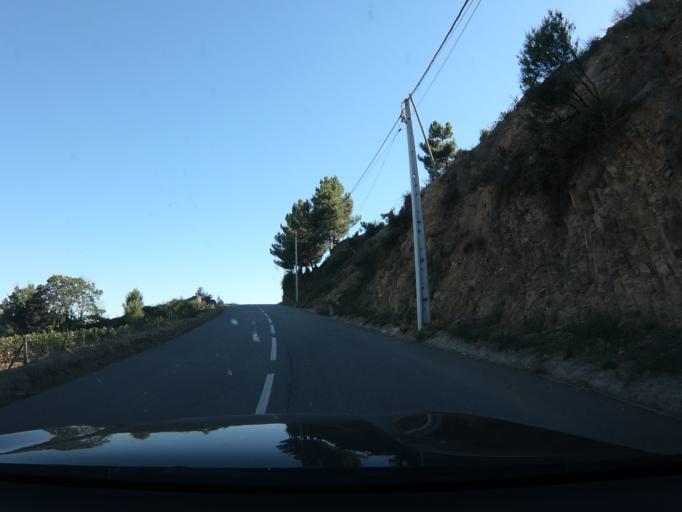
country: PT
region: Vila Real
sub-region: Sabrosa
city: Vilela
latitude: 41.2238
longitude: -7.5629
